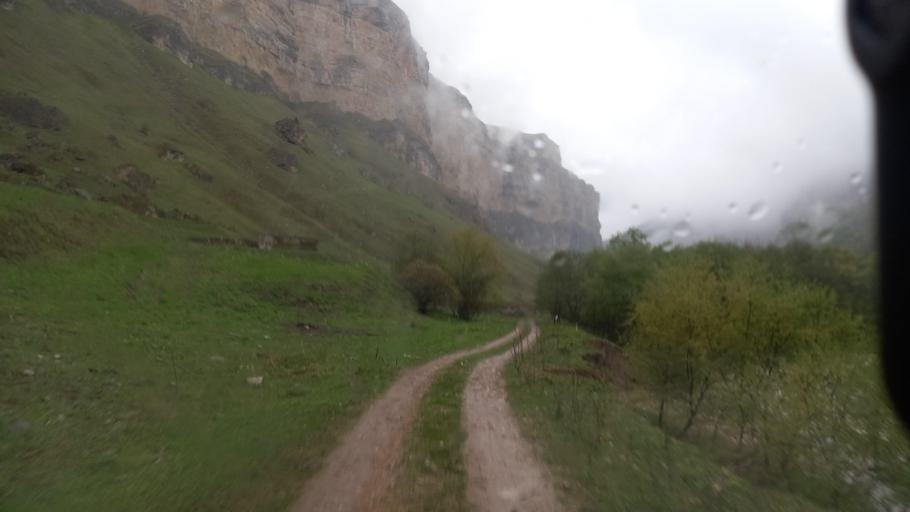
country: RU
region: Kabardino-Balkariya
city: Bylym
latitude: 43.5964
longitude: 42.9571
